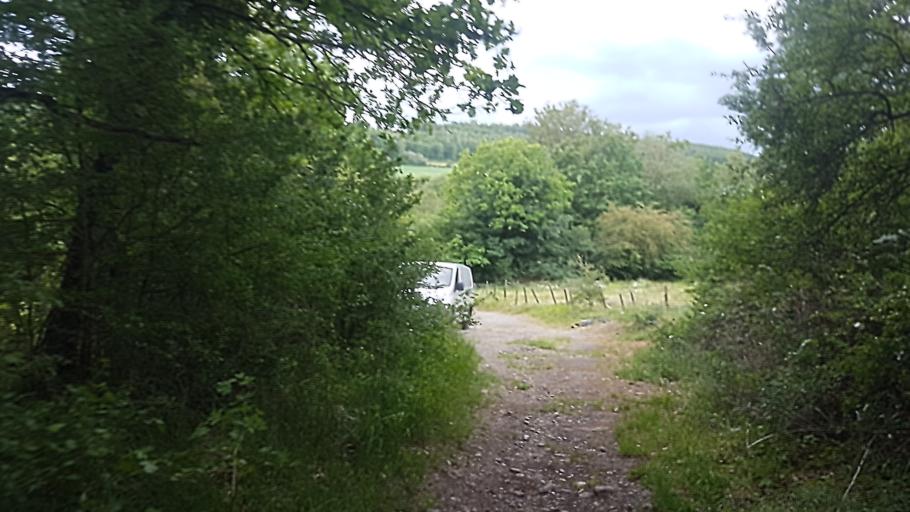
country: BE
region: Wallonia
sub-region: Province de Namur
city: Couvin
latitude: 50.0775
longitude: 4.5965
